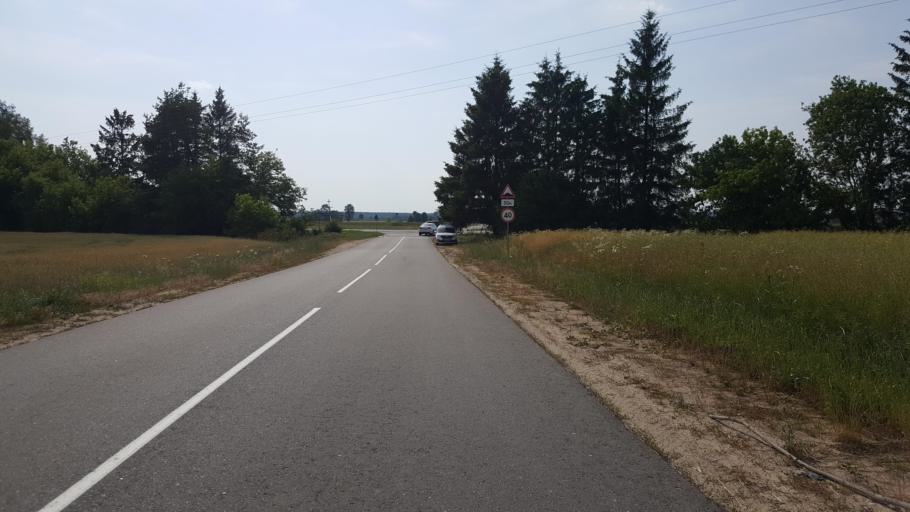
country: BY
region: Brest
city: Kamyanyets
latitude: 52.3704
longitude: 23.7946
